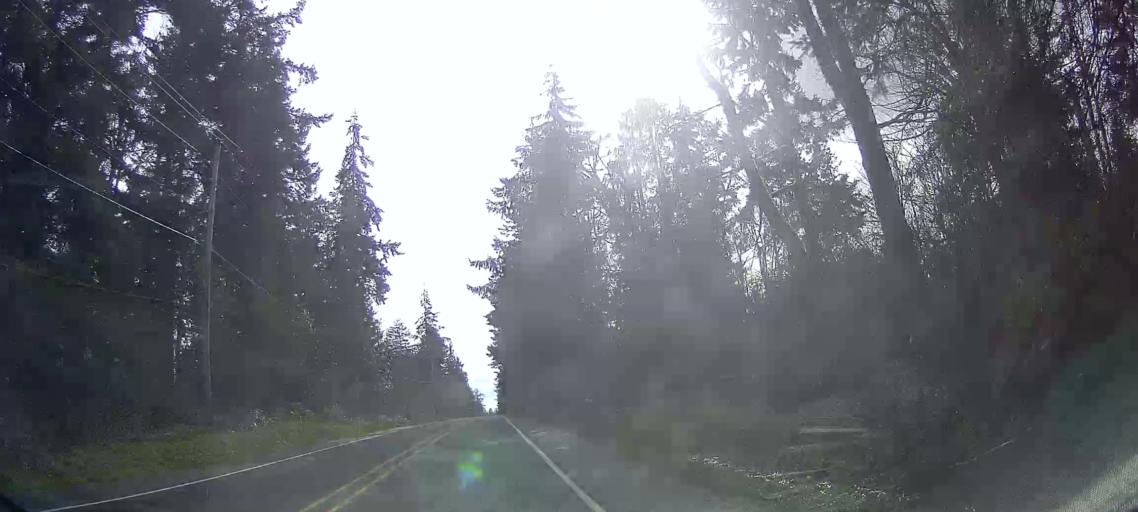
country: US
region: Washington
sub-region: Island County
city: Camano
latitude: 48.1589
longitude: -122.4756
